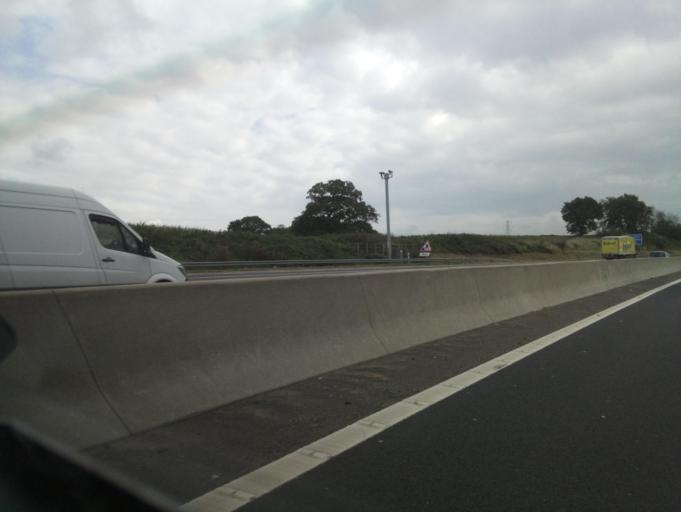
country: GB
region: England
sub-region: Cheshire East
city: Mere
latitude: 53.3108
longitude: -2.4109
